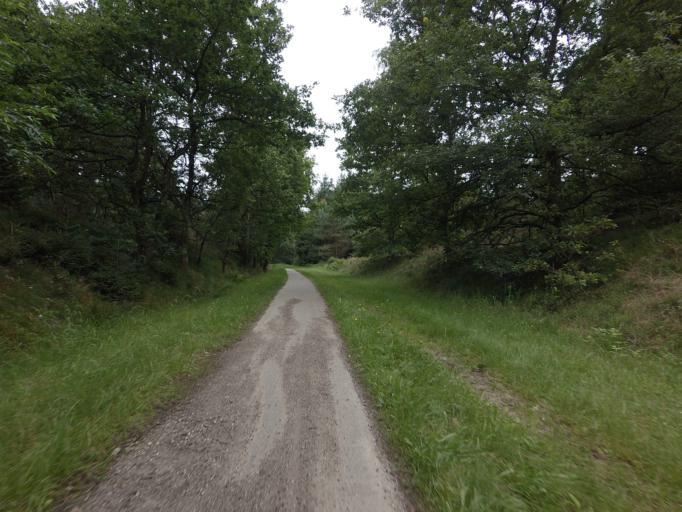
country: DK
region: Central Jutland
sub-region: Silkeborg Kommune
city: Virklund
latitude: 56.0498
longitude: 9.4693
